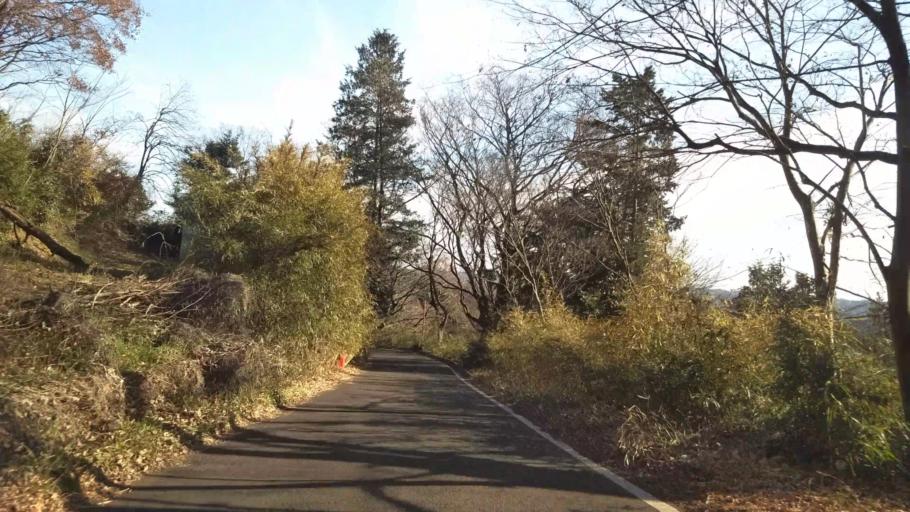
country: JP
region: Kanagawa
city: Hadano
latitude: 35.3699
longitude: 139.2441
